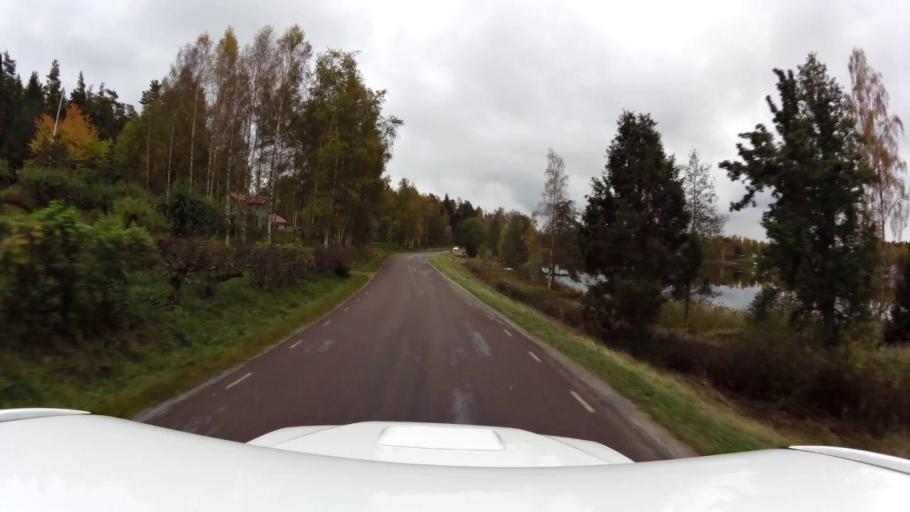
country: SE
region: OEstergoetland
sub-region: Linkopings Kommun
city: Ljungsbro
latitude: 58.5738
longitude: 15.5116
